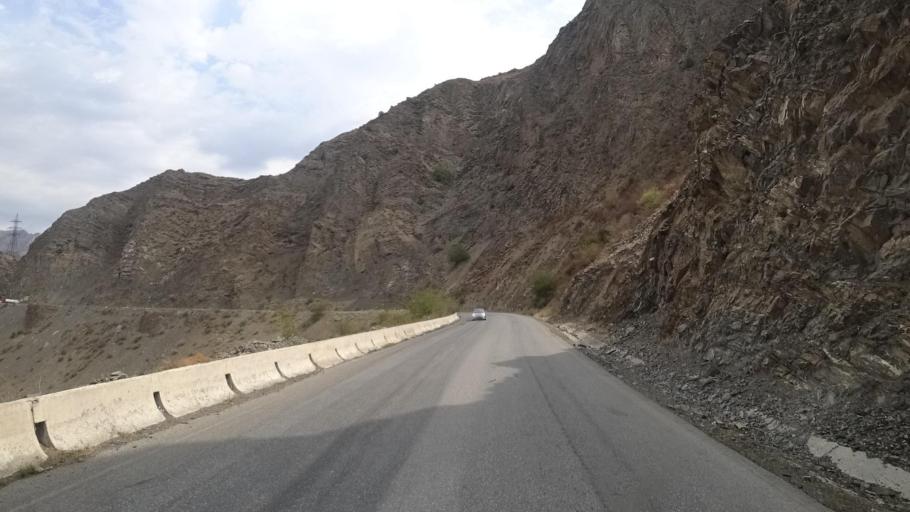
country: KG
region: Jalal-Abad
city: Tash-Kumyr
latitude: 41.4995
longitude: 72.3745
